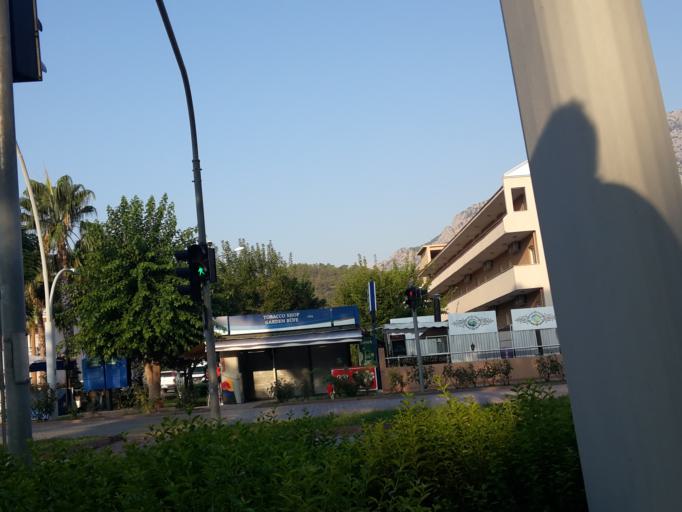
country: TR
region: Antalya
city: Kemer
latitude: 36.6080
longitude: 30.5584
